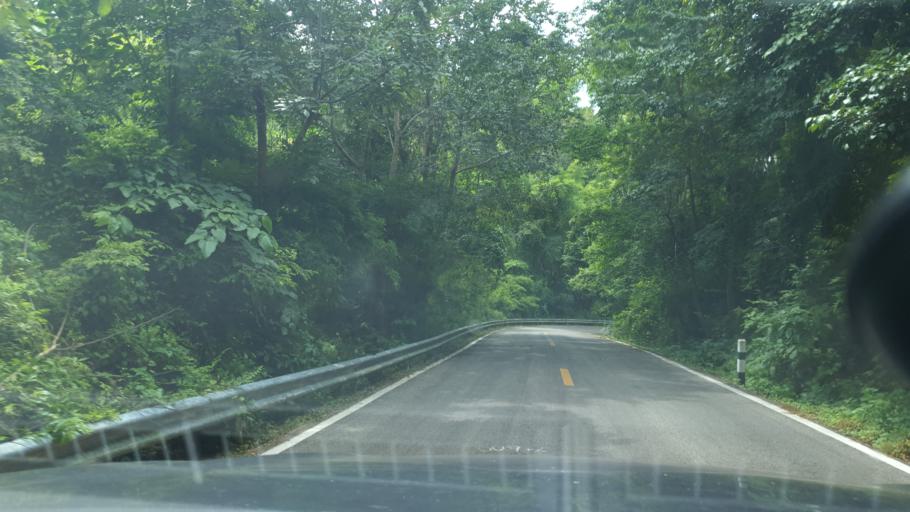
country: TH
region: Lamphun
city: Mae Tha
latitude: 18.4983
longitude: 99.2696
